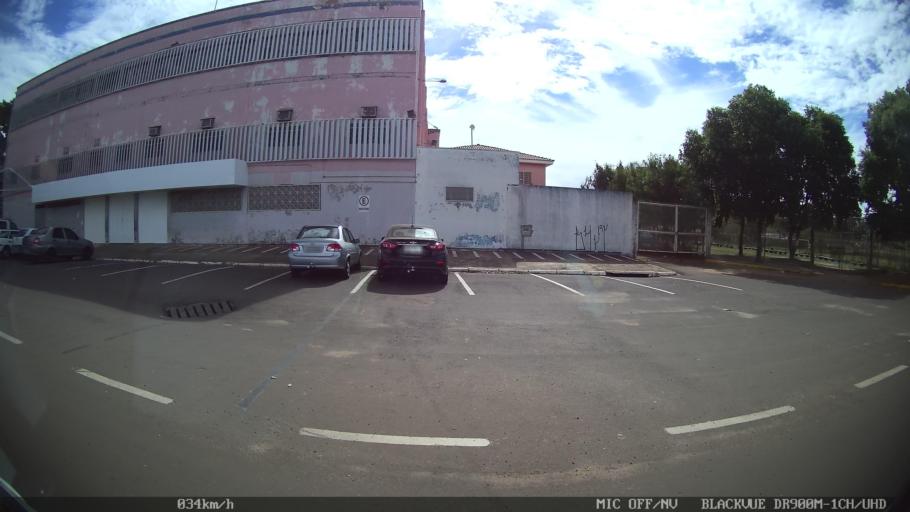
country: BR
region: Sao Paulo
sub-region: Catanduva
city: Catanduva
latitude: -21.1405
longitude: -48.9622
